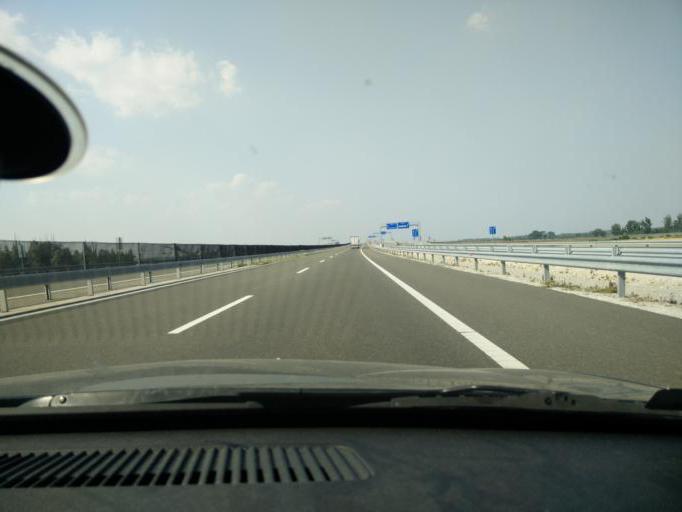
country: HU
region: Tolna
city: Szekszard
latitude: 46.3761
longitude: 18.7523
